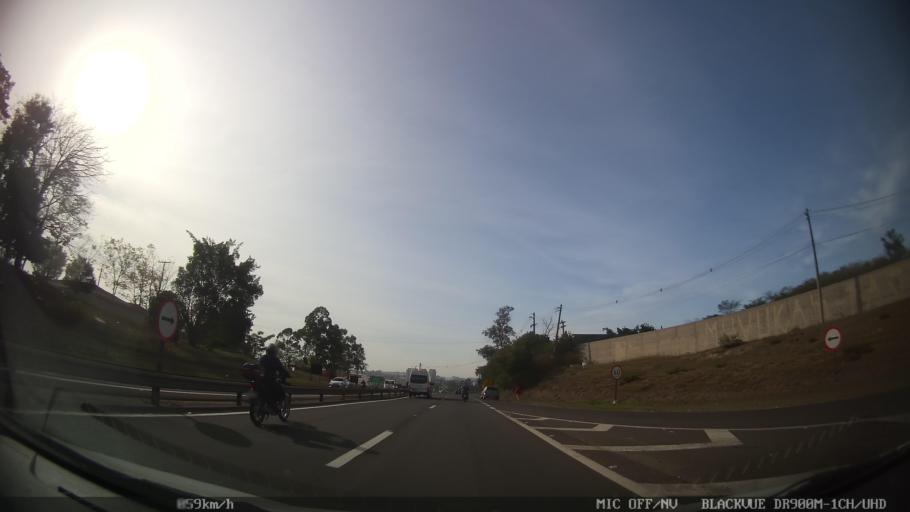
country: BR
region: Sao Paulo
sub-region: Piracicaba
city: Piracicaba
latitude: -22.6836
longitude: -47.6848
